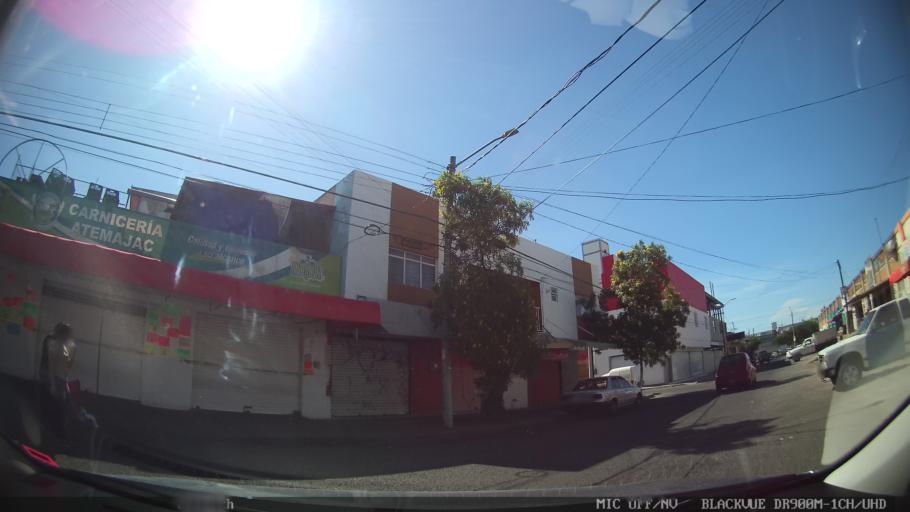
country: MX
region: Jalisco
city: Tlaquepaque
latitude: 20.6599
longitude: -103.2883
